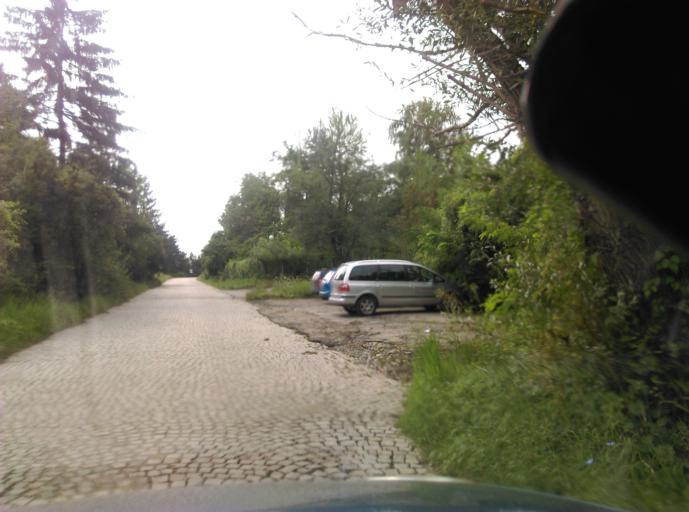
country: BG
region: Sofia-Capital
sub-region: Stolichna Obshtina
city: Sofia
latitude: 42.6050
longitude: 23.3981
